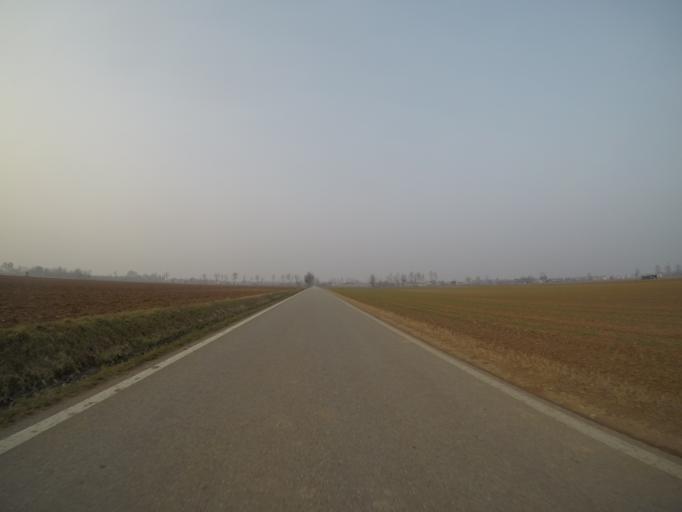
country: IT
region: Veneto
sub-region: Provincia di Treviso
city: Altivole
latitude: 45.7409
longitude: 11.9598
